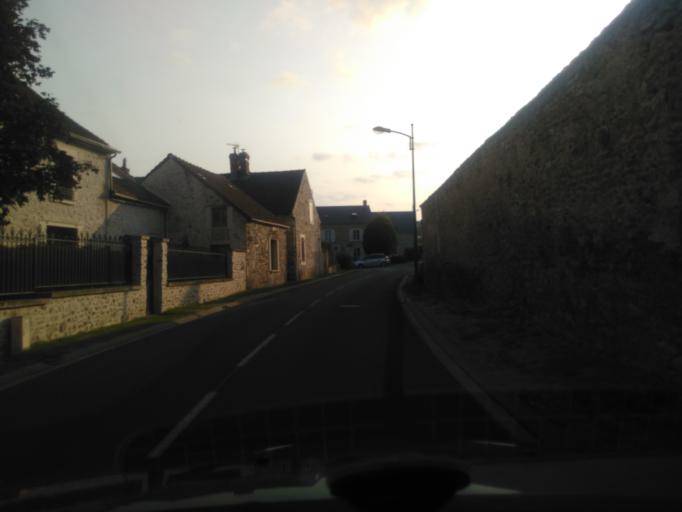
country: FR
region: Champagne-Ardenne
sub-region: Departement de la Marne
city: Fismes
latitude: 49.2346
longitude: 3.6942
